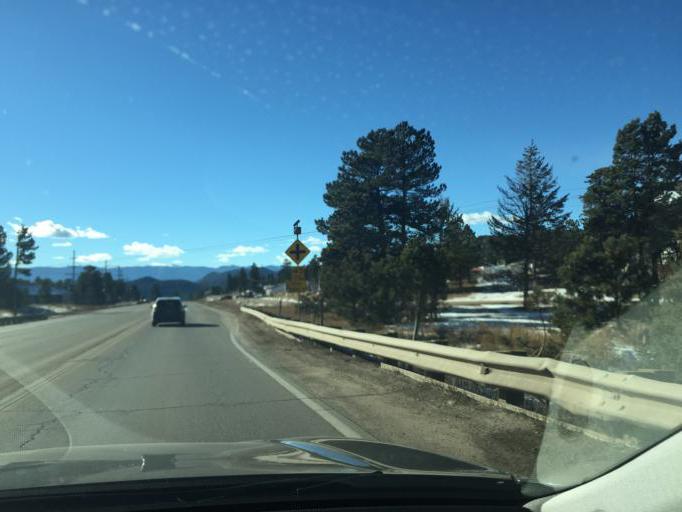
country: US
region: Colorado
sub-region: Jefferson County
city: Evergreen
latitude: 39.4920
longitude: -105.3456
